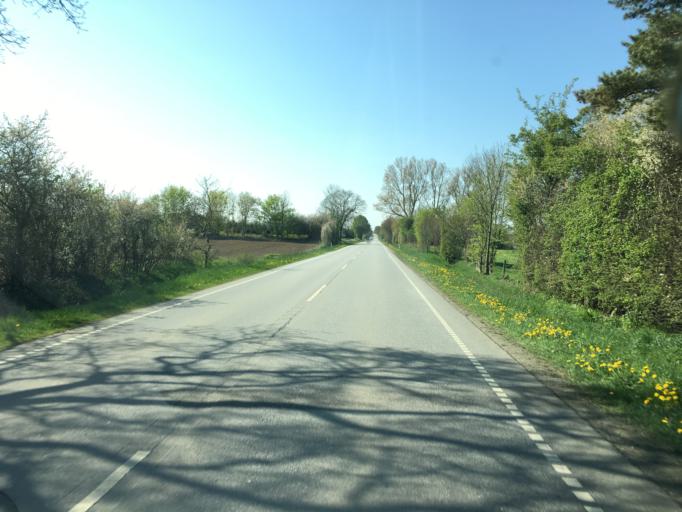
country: DK
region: South Denmark
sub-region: Haderslev Kommune
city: Vojens
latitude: 55.2981
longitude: 9.3768
